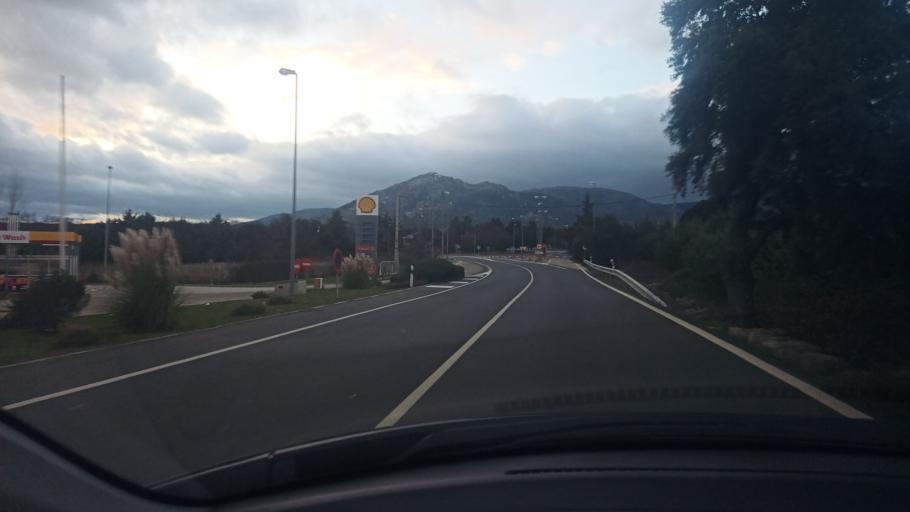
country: ES
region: Madrid
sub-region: Provincia de Madrid
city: El Escorial
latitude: 40.5439
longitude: -4.1095
